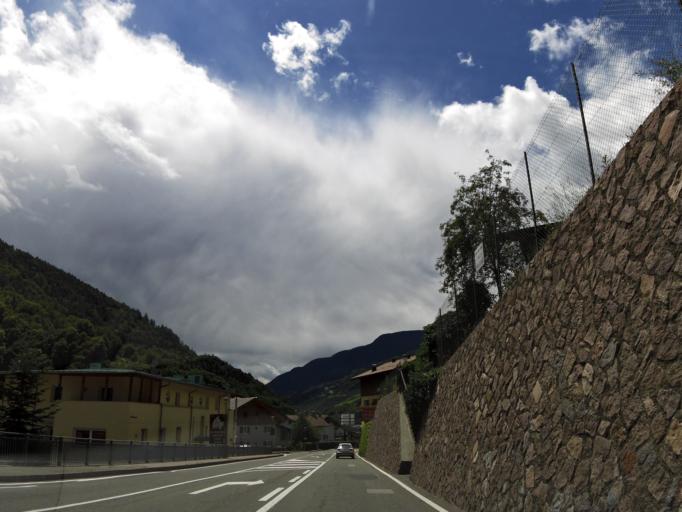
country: IT
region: Trentino-Alto Adige
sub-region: Bolzano
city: Chiusa
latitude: 46.6374
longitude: 11.5603
